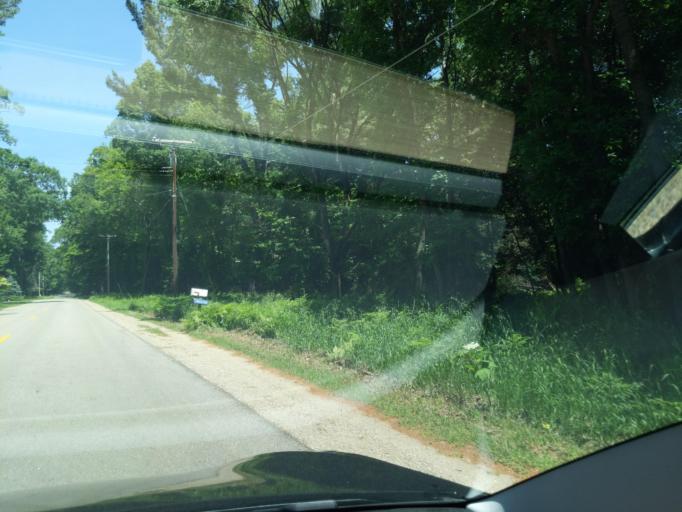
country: US
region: Michigan
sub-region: Muskegon County
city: Montague
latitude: 43.3843
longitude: -86.4160
